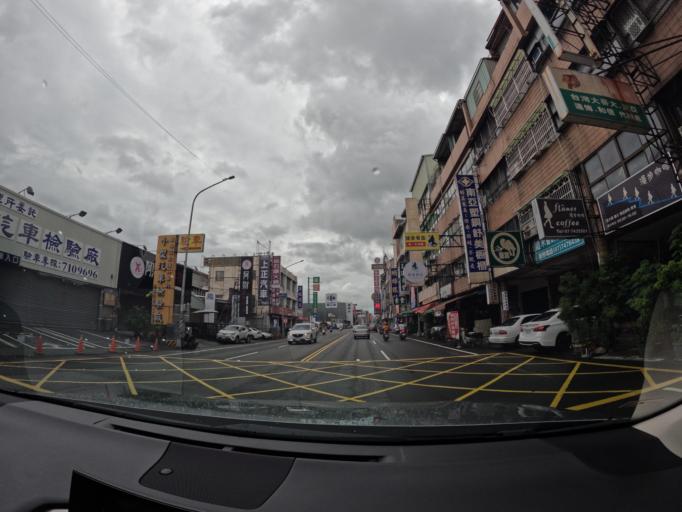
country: TW
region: Taiwan
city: Fengshan
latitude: 22.6280
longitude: 120.3464
